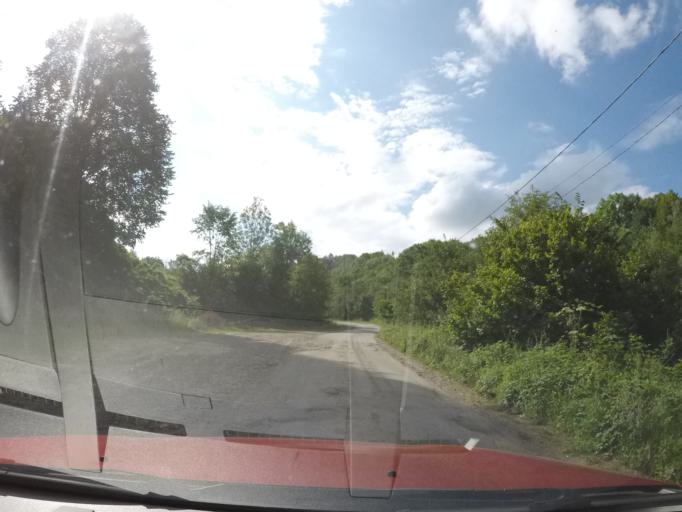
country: UA
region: Zakarpattia
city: Velykyi Bereznyi
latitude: 48.9470
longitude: 22.6781
